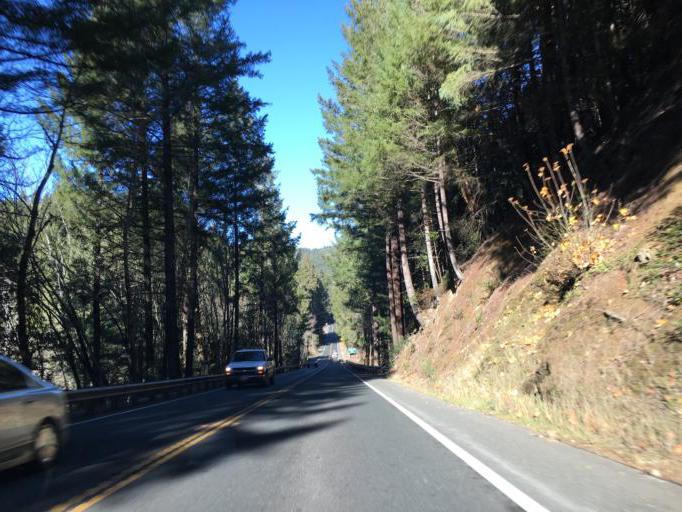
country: US
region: California
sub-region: Mendocino County
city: Brooktrails
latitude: 39.4786
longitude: -123.3633
